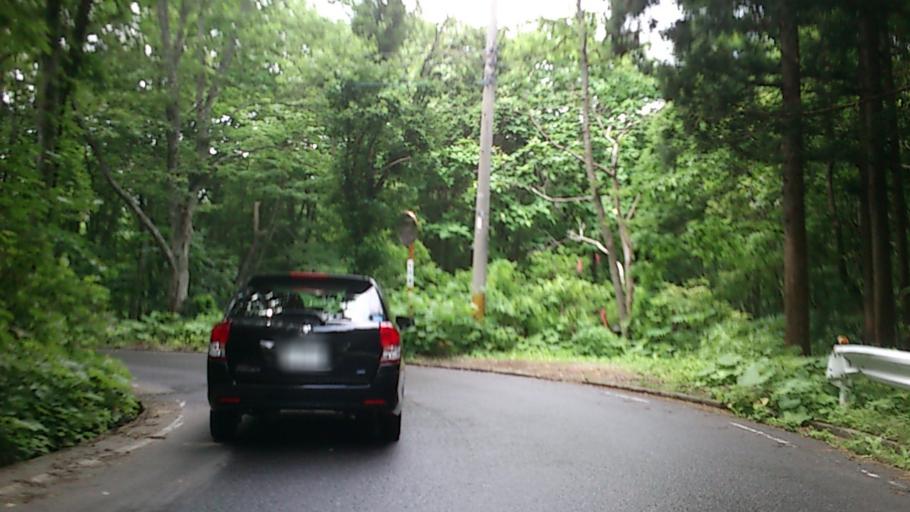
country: JP
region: Aomori
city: Hirosaki
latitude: 40.5178
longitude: 140.1926
